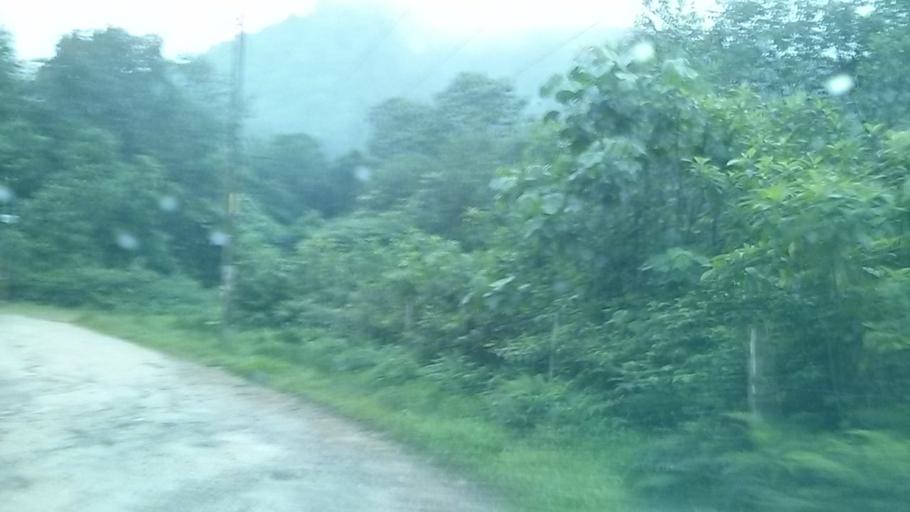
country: CR
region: San Jose
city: Ipis
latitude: 10.0211
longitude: -83.9430
